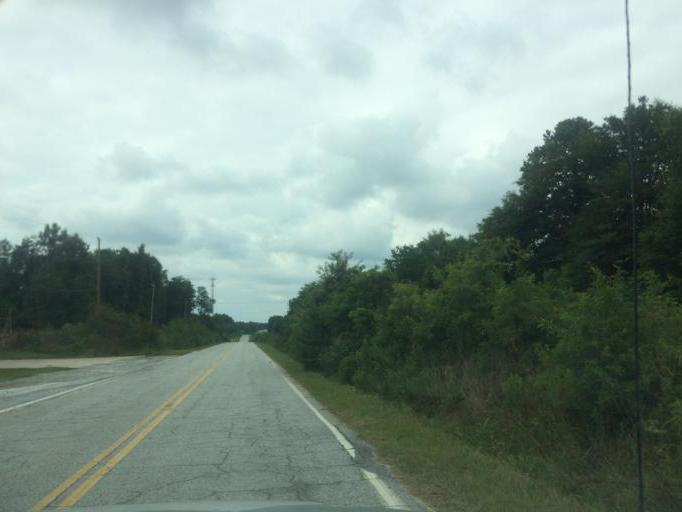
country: US
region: South Carolina
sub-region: Greenville County
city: Gantt
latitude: 34.7922
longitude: -82.4250
